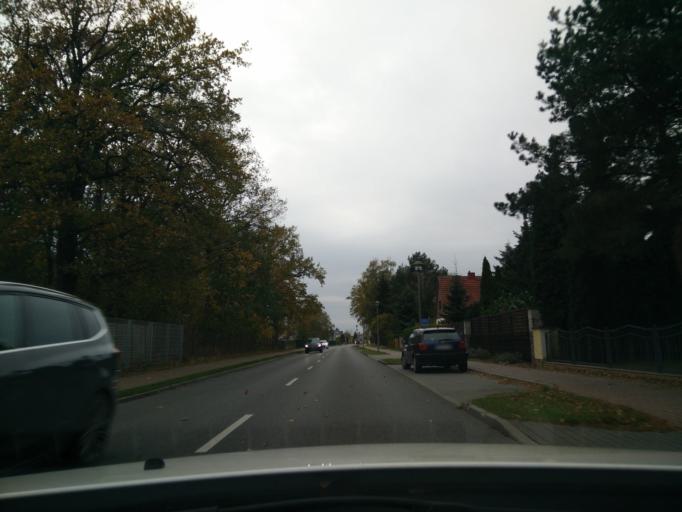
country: DE
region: Brandenburg
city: Velten
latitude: 52.6631
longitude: 13.1520
